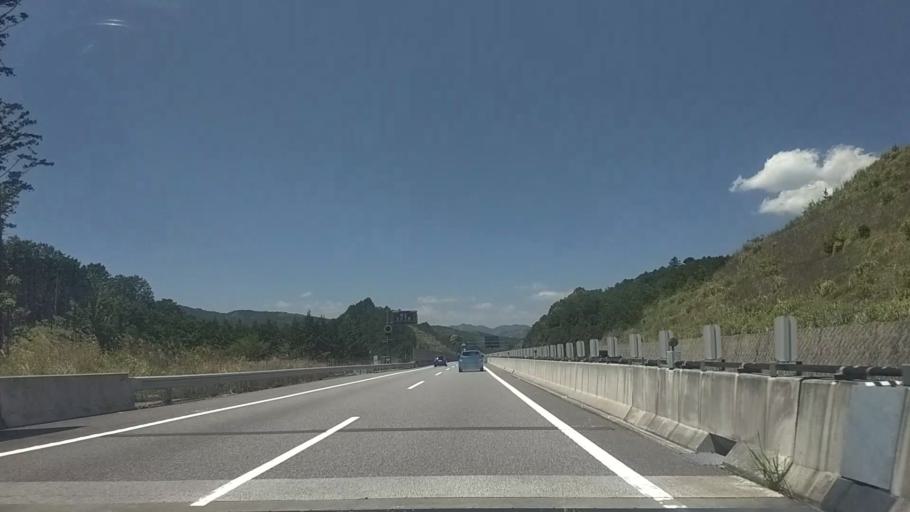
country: JP
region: Aichi
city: Shinshiro
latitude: 34.8972
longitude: 137.6252
